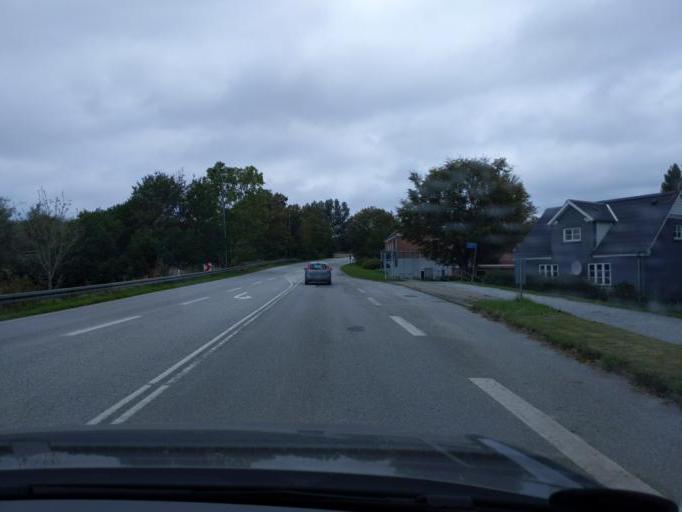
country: DK
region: North Denmark
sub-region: Mariagerfjord Kommune
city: Hobro
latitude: 56.5694
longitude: 9.8215
